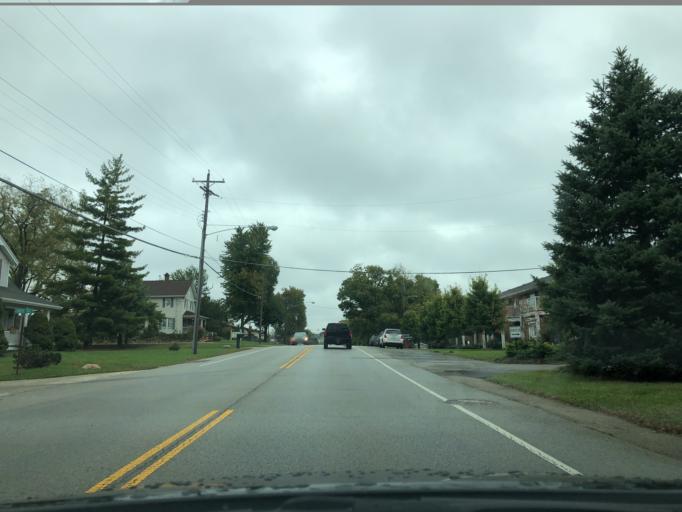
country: US
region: Ohio
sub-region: Hamilton County
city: Sharonville
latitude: 39.2781
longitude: -84.4086
